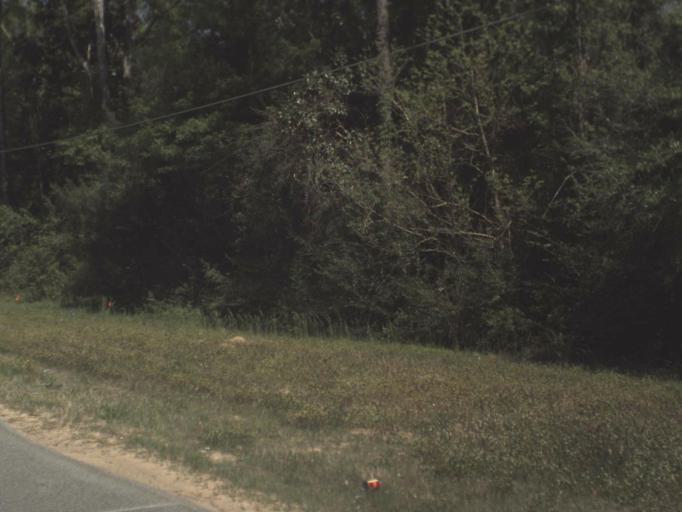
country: US
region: Florida
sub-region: Okaloosa County
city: Crestview
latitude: 30.7492
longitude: -86.6390
